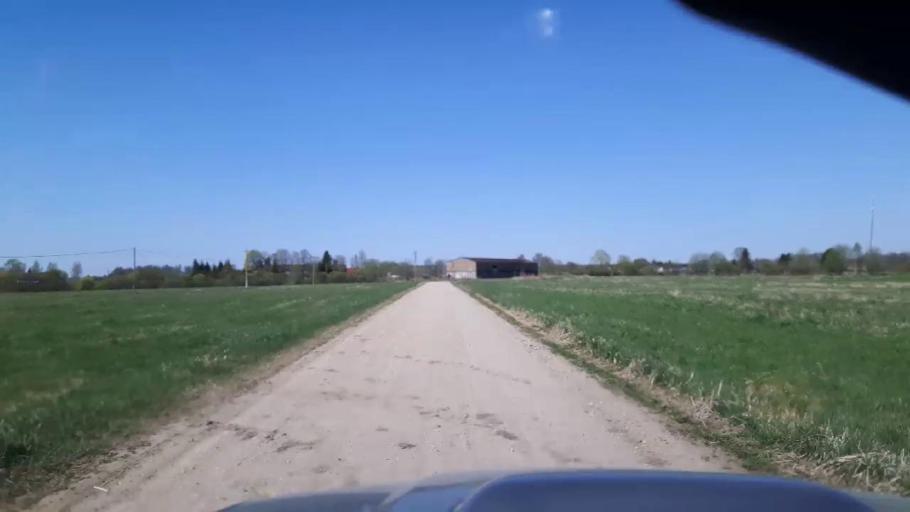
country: EE
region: Paernumaa
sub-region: Sindi linn
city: Sindi
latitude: 58.4451
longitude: 24.7797
